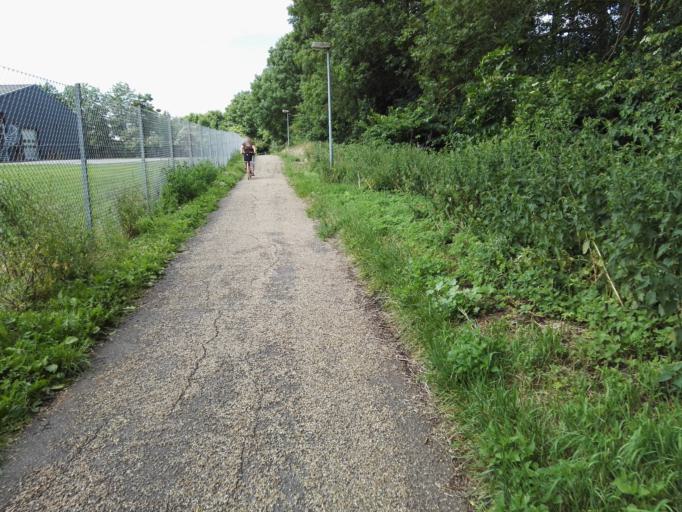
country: DK
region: Capital Region
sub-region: Frederikssund Kommune
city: Slangerup
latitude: 55.8459
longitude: 12.1816
